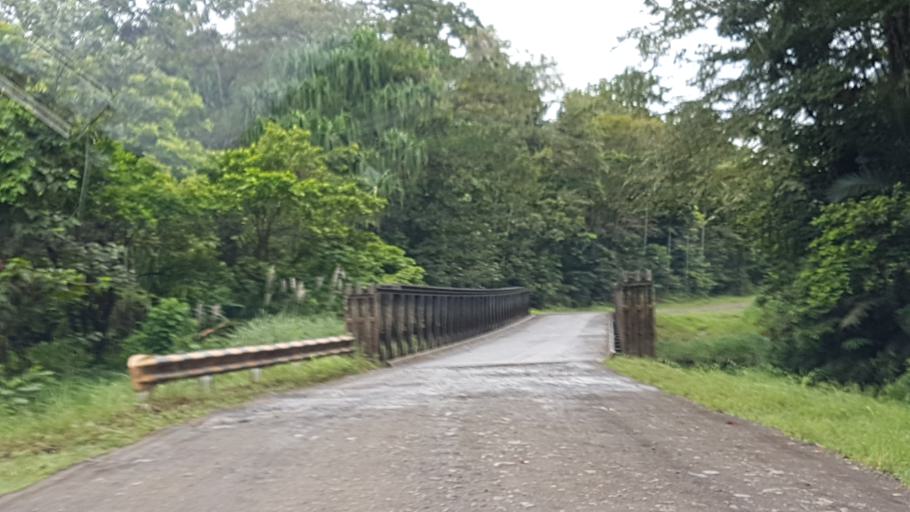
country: PG
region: Milne Bay
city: Alotau
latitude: -10.3386
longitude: 150.6059
